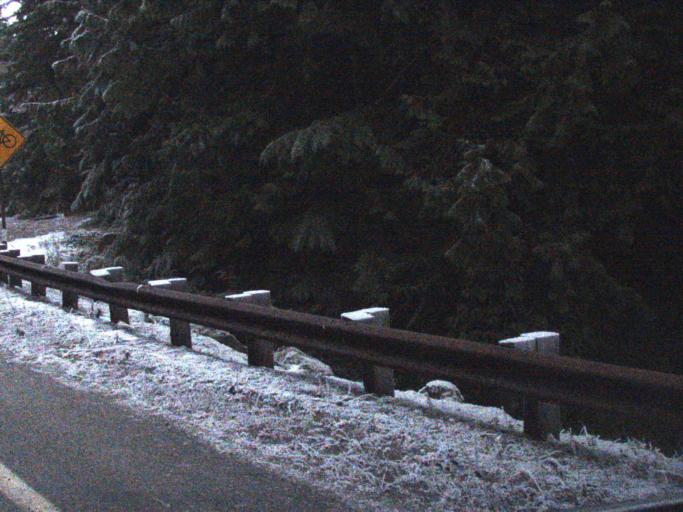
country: US
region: Washington
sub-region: Snohomish County
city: Darrington
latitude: 48.6898
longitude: -121.1032
